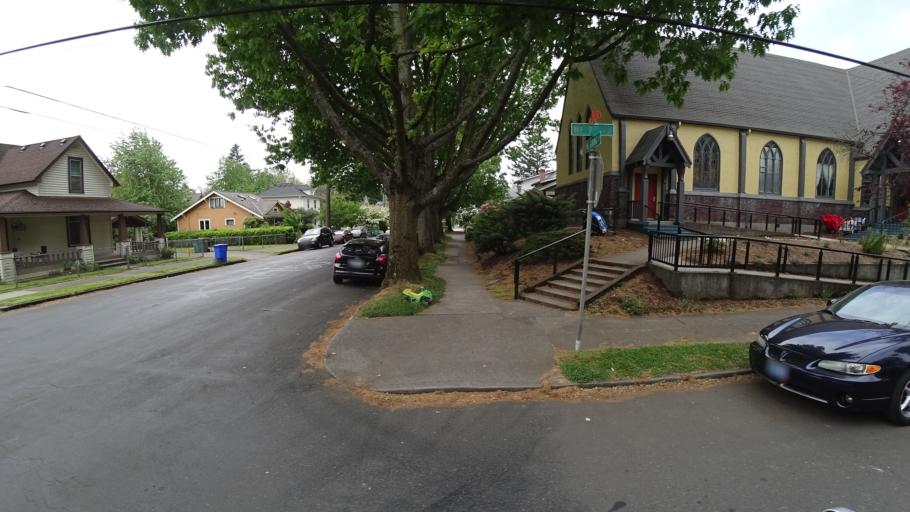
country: US
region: Oregon
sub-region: Multnomah County
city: Portland
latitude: 45.5564
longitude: -122.6566
